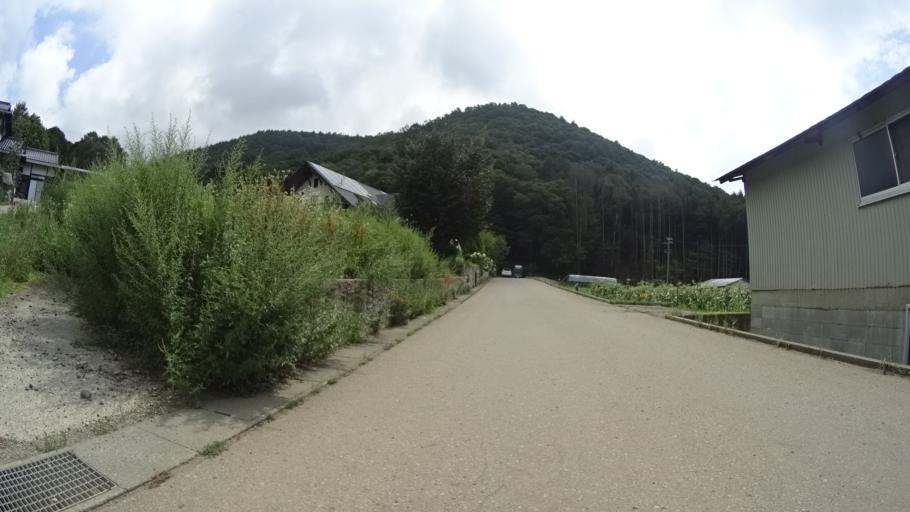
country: JP
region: Yamanashi
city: Nirasaki
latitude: 35.9170
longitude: 138.4523
